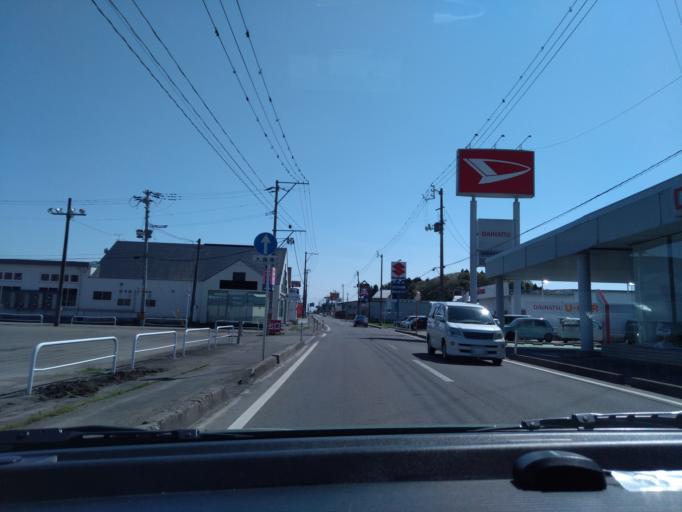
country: JP
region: Akita
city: Kakunodatemachi
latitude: 39.5894
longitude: 140.5733
